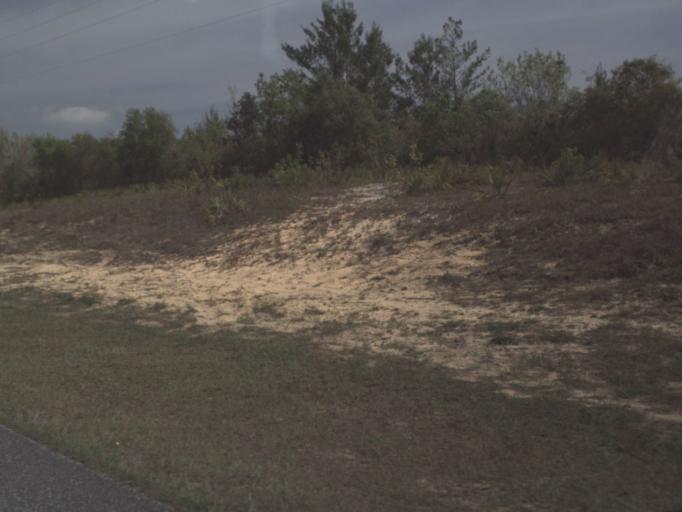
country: US
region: Florida
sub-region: Lake County
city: Astor
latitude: 29.1666
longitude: -81.6417
